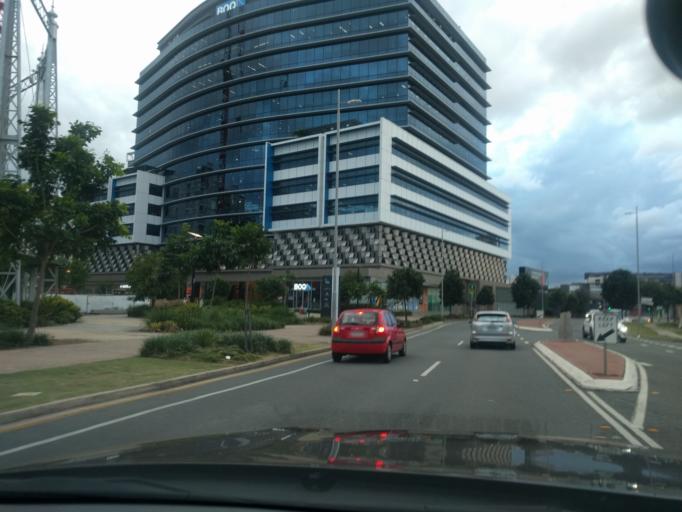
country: AU
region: Queensland
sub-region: Brisbane
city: Fortitude Valley
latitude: -27.4501
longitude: 153.0434
